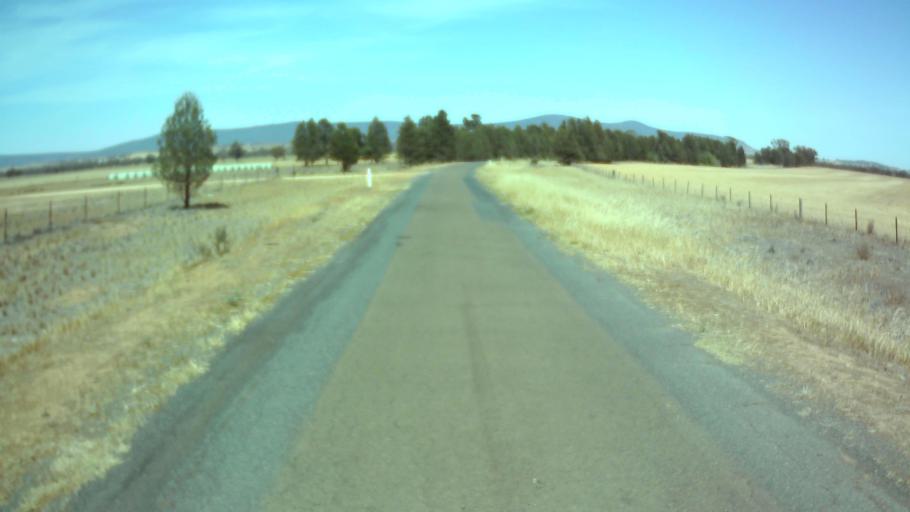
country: AU
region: New South Wales
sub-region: Weddin
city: Grenfell
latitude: -33.8707
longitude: 148.1048
